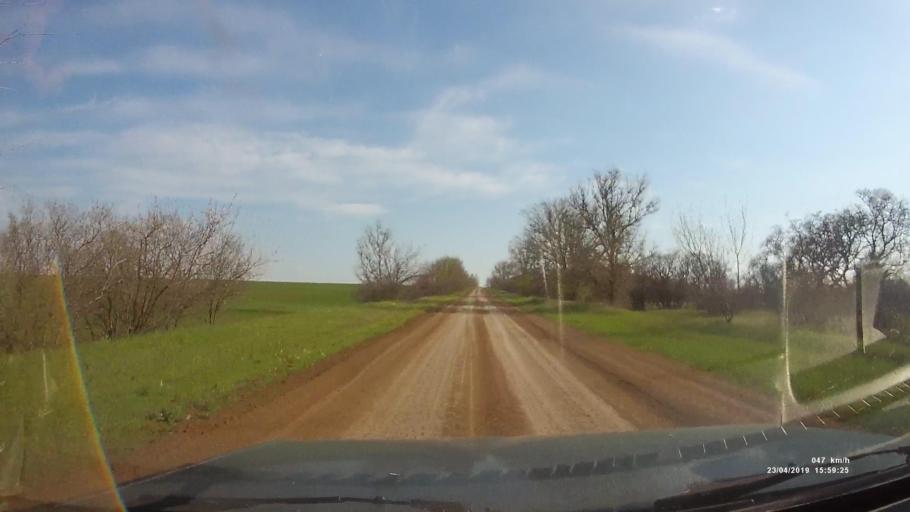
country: RU
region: Rostov
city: Remontnoye
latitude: 46.5170
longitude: 43.1096
